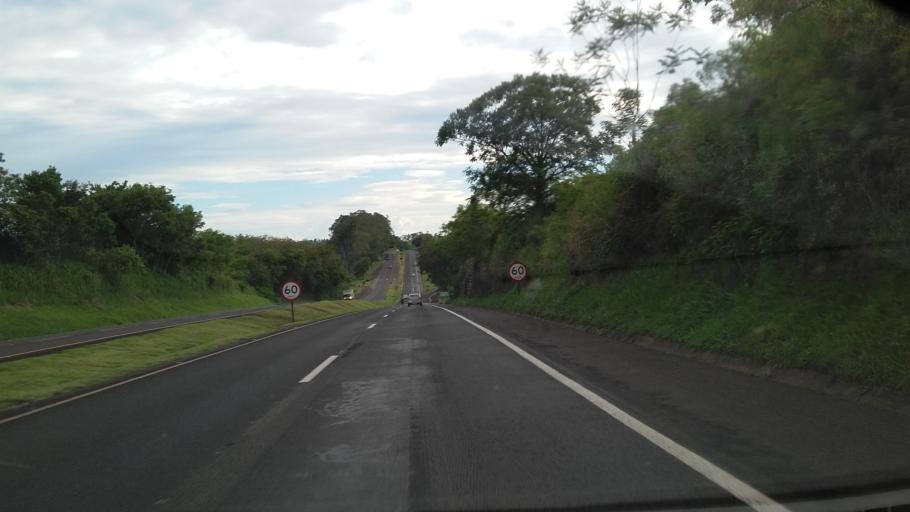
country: BR
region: Parana
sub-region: Paicandu
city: Paicandu
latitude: -23.5178
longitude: -52.0281
